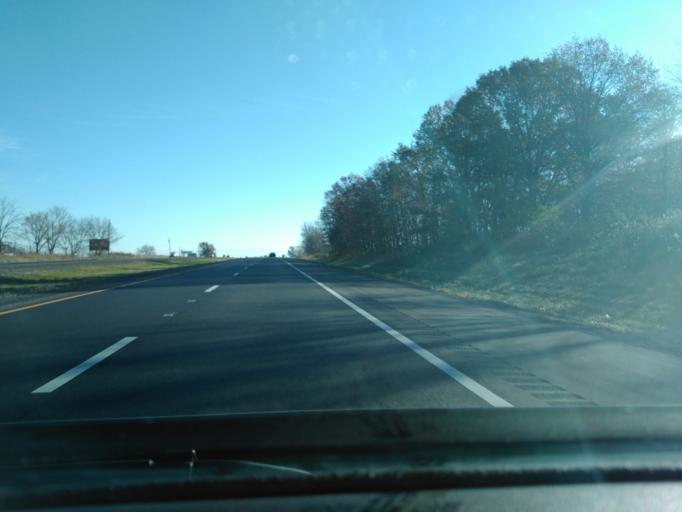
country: US
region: Illinois
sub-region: Madison County
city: Highland
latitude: 38.7863
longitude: -89.6530
